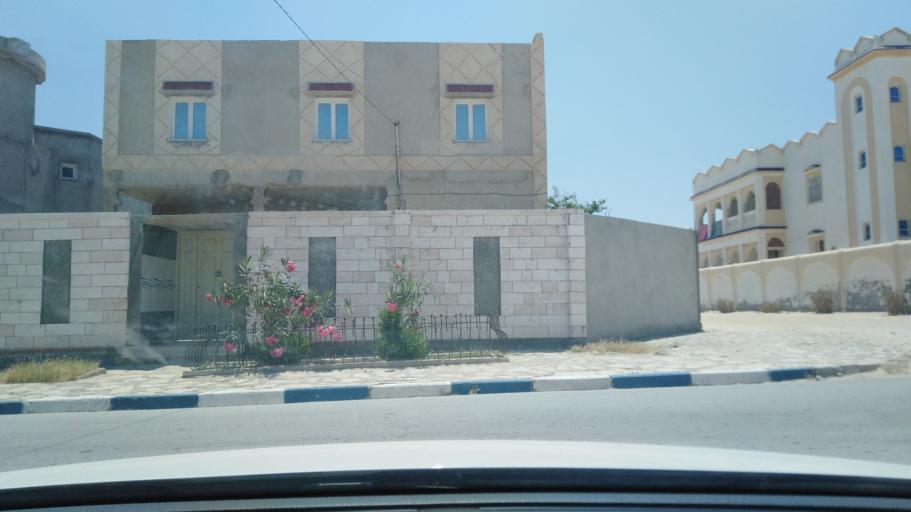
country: TN
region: Qabis
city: Gabes
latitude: 33.9514
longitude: 10.0696
